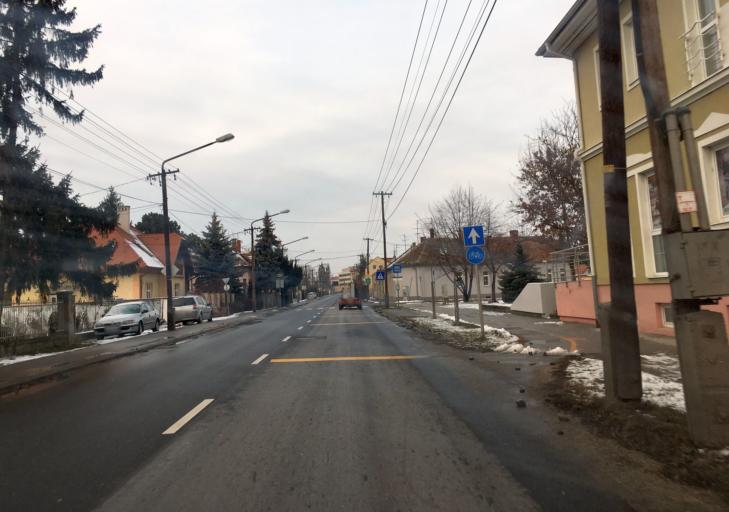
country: HU
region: Gyor-Moson-Sopron
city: Mosonmagyarovar
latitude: 47.8687
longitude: 17.2685
